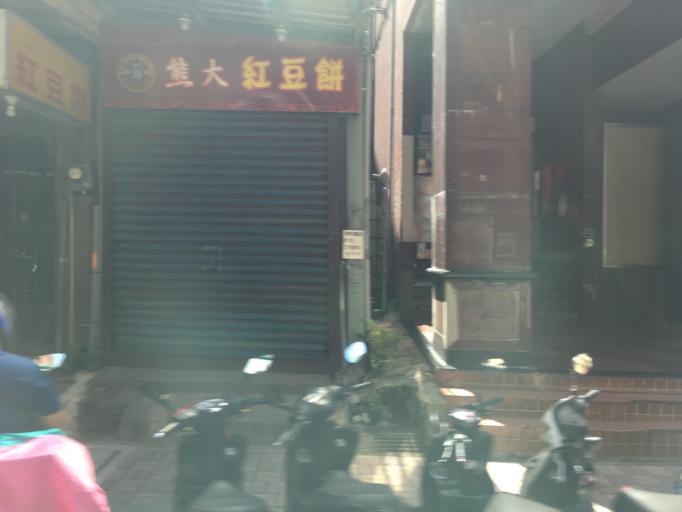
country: TW
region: Taipei
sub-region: Taipei
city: Banqiao
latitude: 25.0488
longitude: 121.4273
